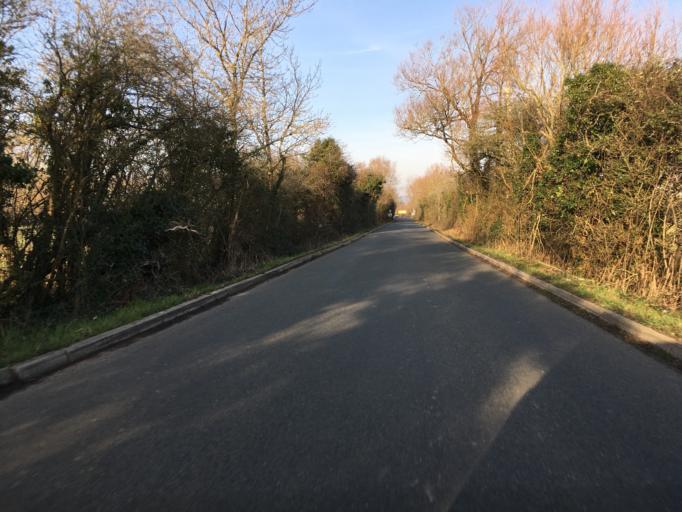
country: GB
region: Wales
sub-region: Newport
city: Bishton
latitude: 51.5677
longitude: -2.8691
